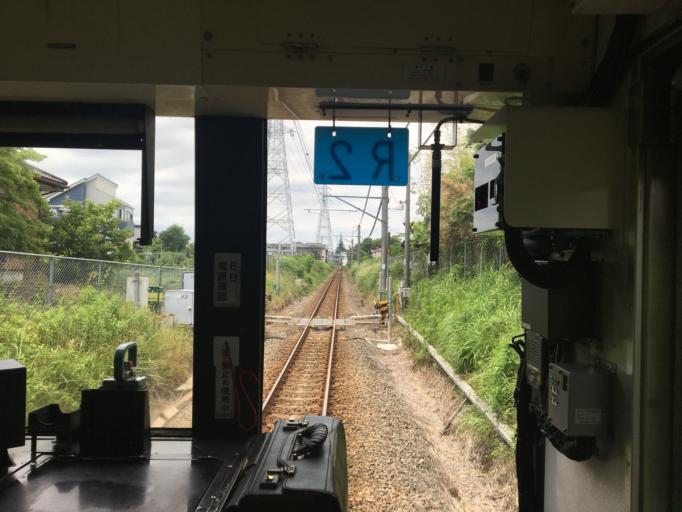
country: JP
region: Kanagawa
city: Zama
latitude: 35.5232
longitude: 139.3783
